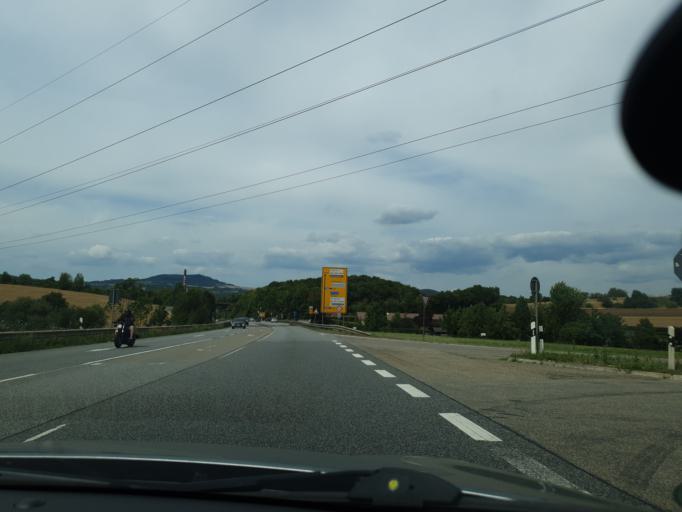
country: DE
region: Rheinland-Pfalz
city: Mayen
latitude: 50.3146
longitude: 7.2397
